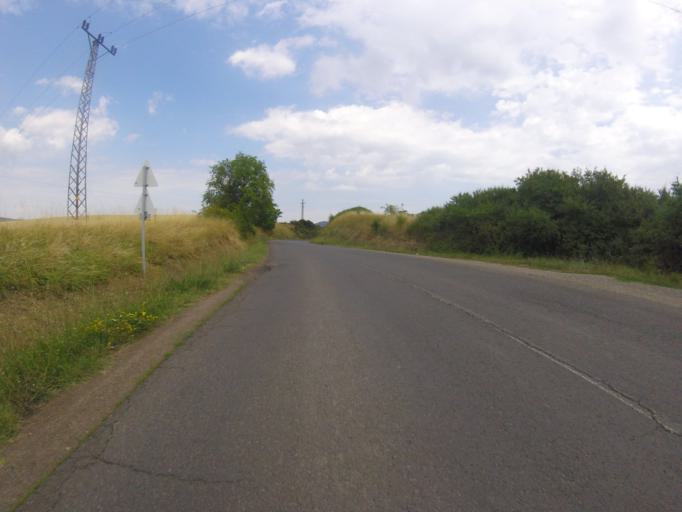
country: HU
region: Nograd
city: Tar
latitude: 47.9394
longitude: 19.7232
